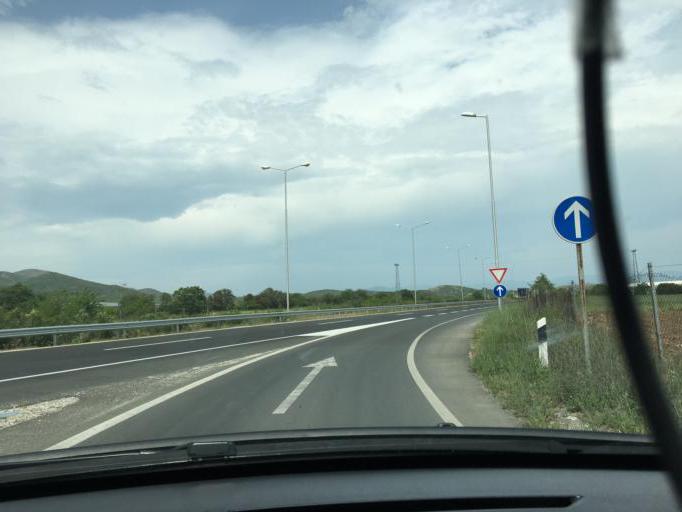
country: MK
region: Gevgelija
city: Gevgelija
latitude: 41.2053
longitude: 22.4959
